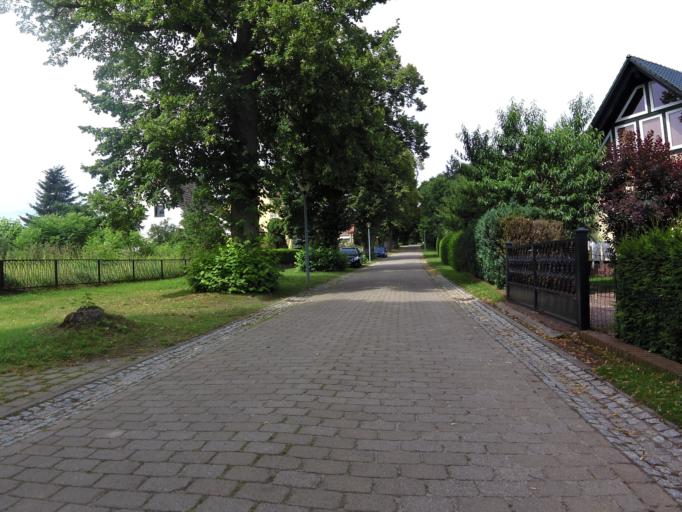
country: DE
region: Mecklenburg-Vorpommern
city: Loitz
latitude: 53.3397
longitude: 13.4318
